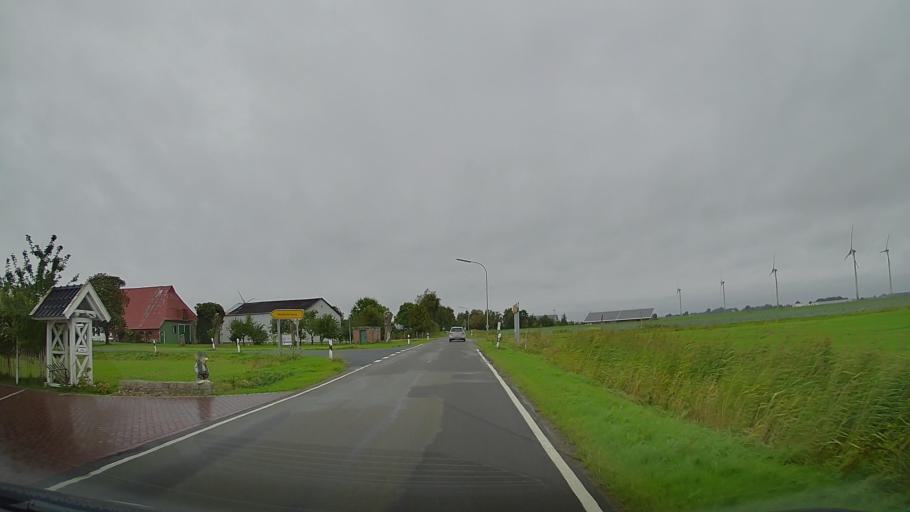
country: DE
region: Schleswig-Holstein
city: Neufeld
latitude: 53.9151
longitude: 8.9994
